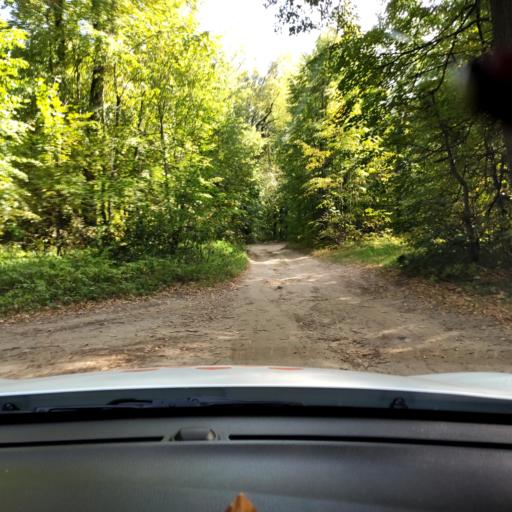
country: RU
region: Tatarstan
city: Staroye Arakchino
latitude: 55.8065
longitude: 49.0160
